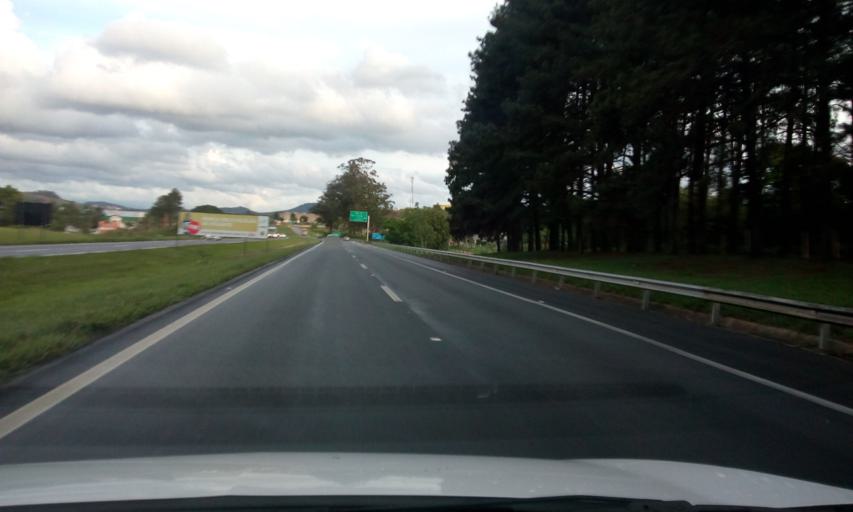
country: BR
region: Sao Paulo
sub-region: Bom Jesus Dos Perdoes
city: Bom Jesus dos Perdoes
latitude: -23.1133
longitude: -46.4902
